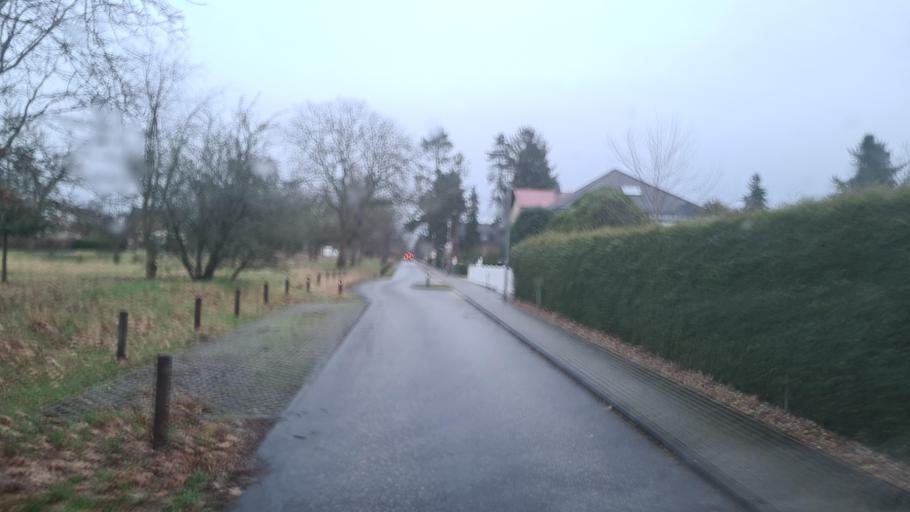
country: DE
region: Brandenburg
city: Teltow
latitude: 52.3884
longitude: 13.2881
